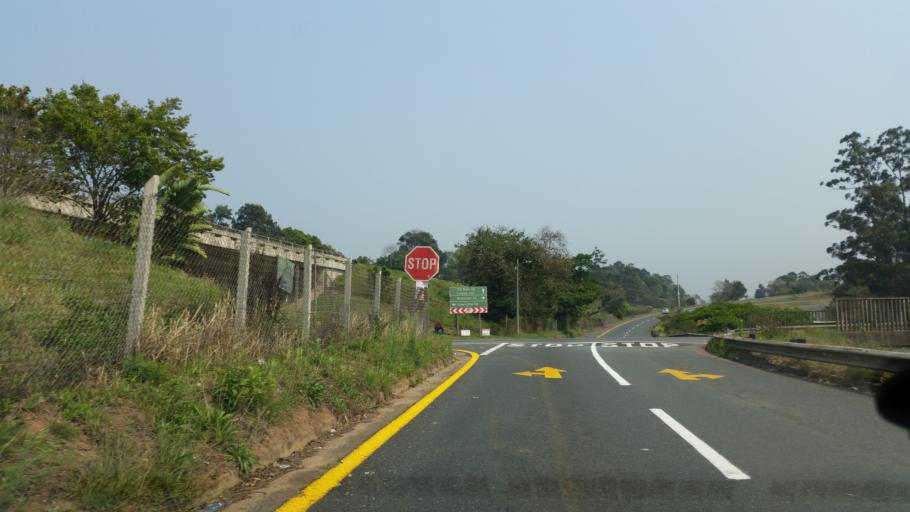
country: ZA
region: KwaZulu-Natal
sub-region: eThekwini Metropolitan Municipality
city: Berea
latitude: -29.8363
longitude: 30.9024
